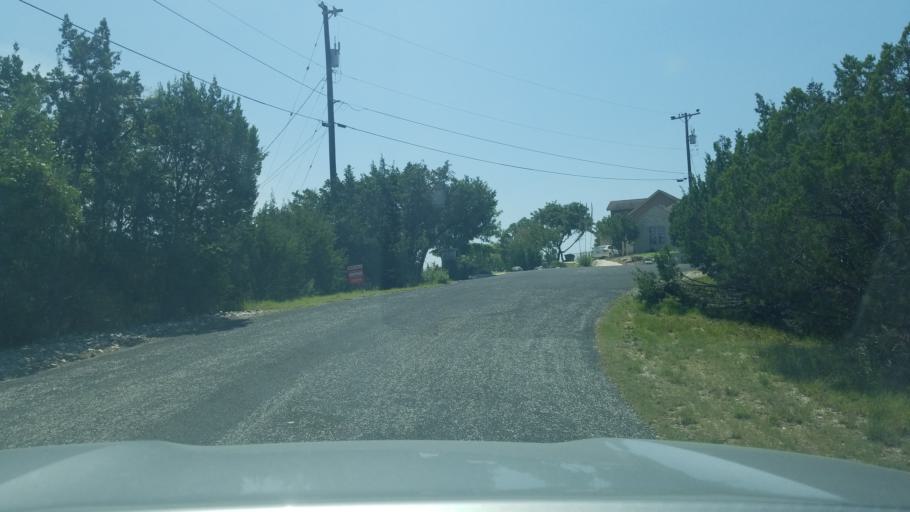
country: US
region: Texas
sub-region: Bexar County
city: Timberwood Park
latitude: 29.6987
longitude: -98.4838
